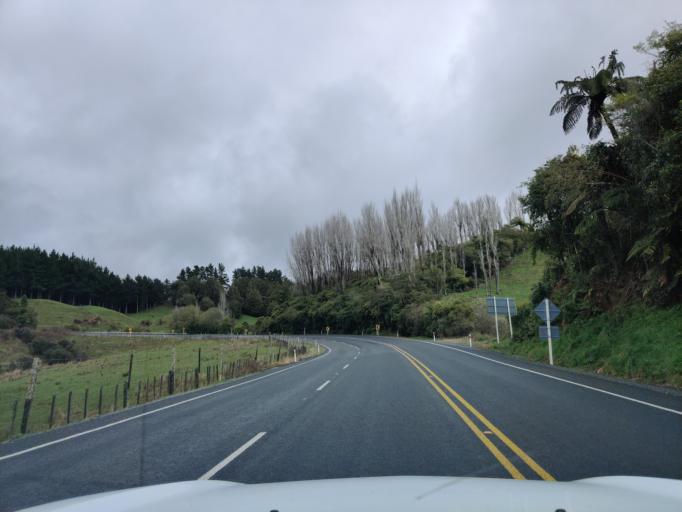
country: NZ
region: Waikato
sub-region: Otorohanga District
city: Otorohanga
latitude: -38.6353
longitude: 175.2065
